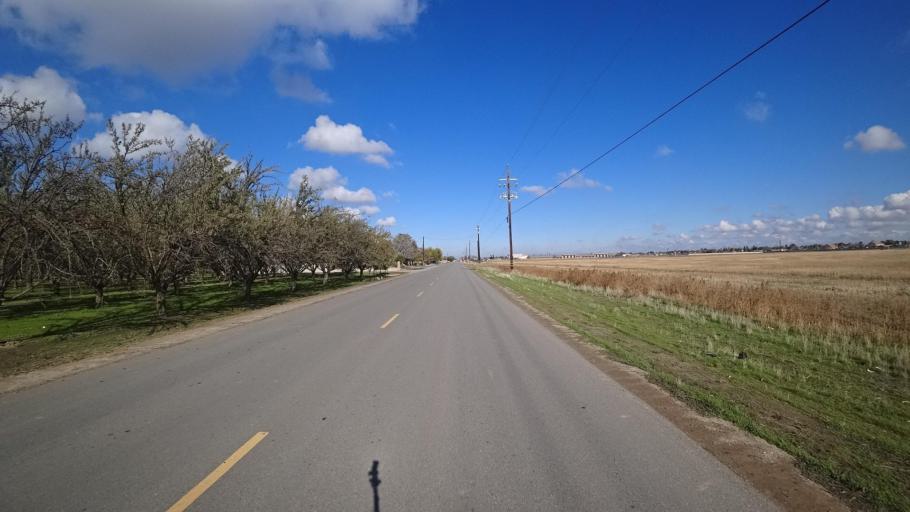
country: US
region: California
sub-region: Kern County
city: McFarland
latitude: 35.6621
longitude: -119.2400
